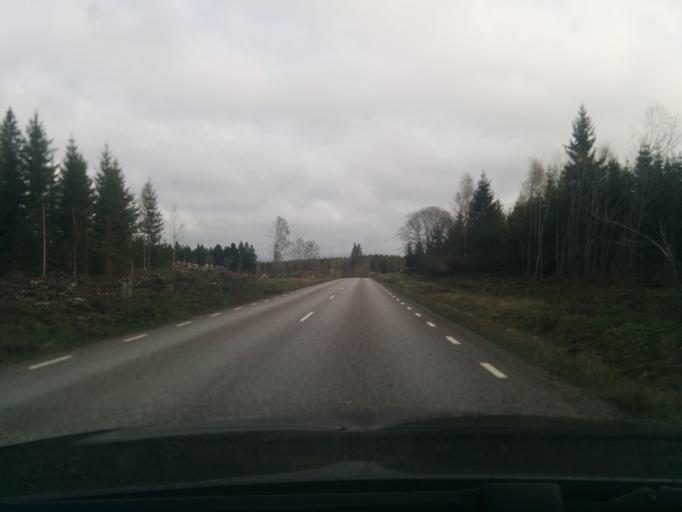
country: SE
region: Uppsala
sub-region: Tierps Kommun
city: Orbyhus
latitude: 60.2081
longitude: 17.6987
